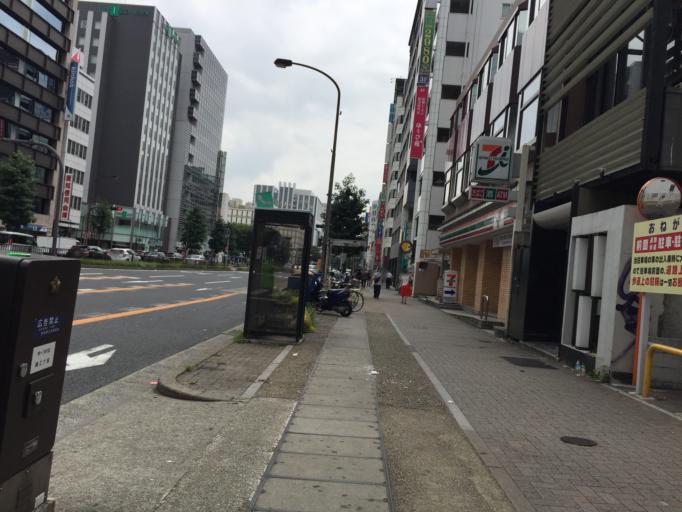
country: JP
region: Aichi
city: Nagoya-shi
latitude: 35.1715
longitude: 136.9065
